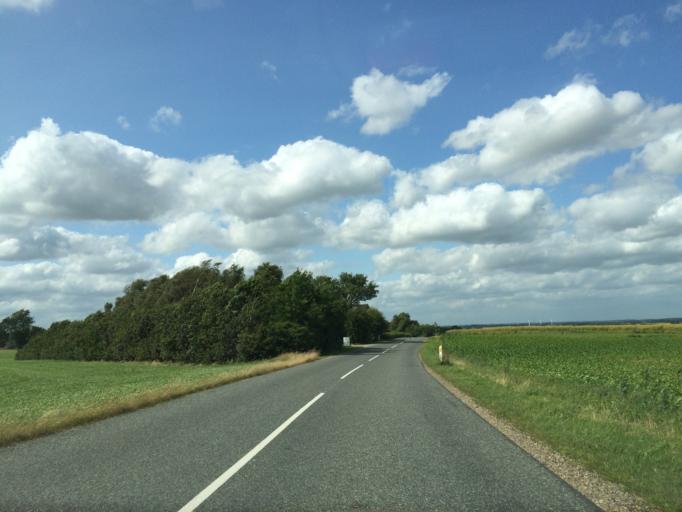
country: DK
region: Central Jutland
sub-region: Skanderborg Kommune
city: Ry
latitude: 56.2033
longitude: 9.7559
